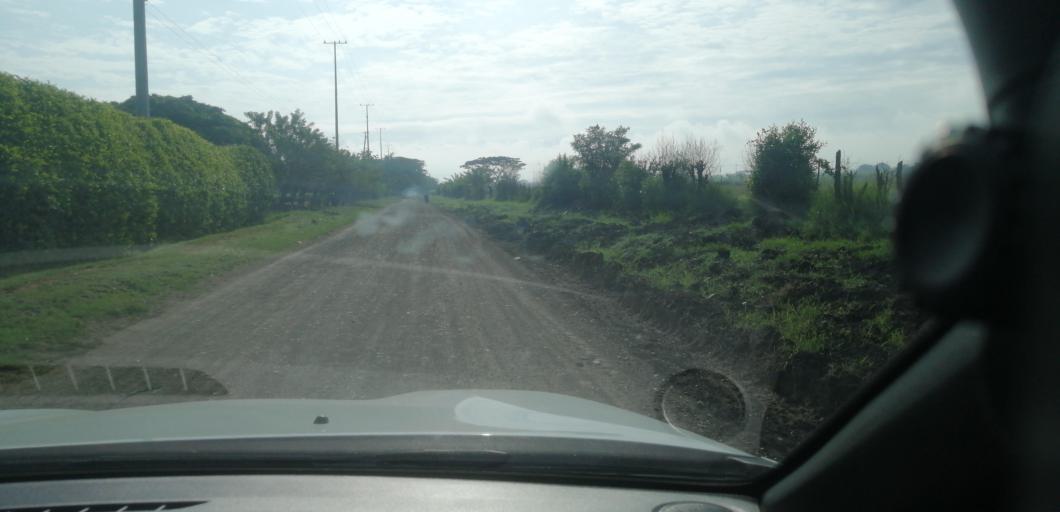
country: CO
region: Valle del Cauca
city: Yumbo
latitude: 3.5793
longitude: -76.4161
